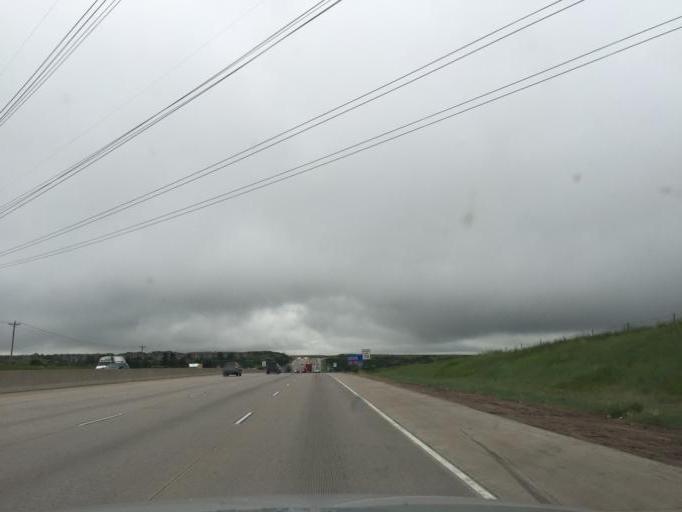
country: US
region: Colorado
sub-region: Douglas County
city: Castle Pines
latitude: 39.4580
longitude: -104.8748
